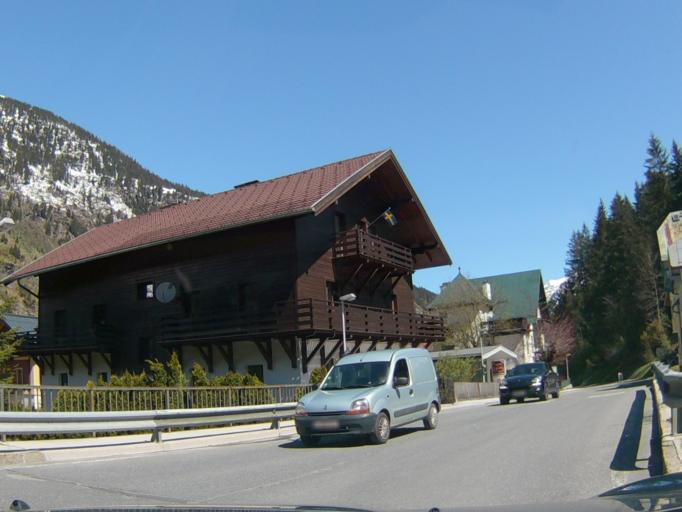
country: AT
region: Salzburg
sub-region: Politischer Bezirk Sankt Johann im Pongau
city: Bad Gastein
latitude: 47.0871
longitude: 13.1196
